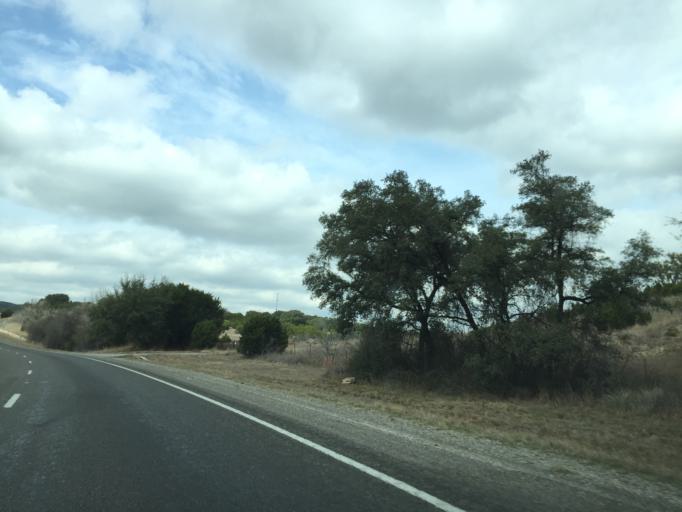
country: US
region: Texas
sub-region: Travis County
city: Briarcliff
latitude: 30.4244
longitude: -98.1300
